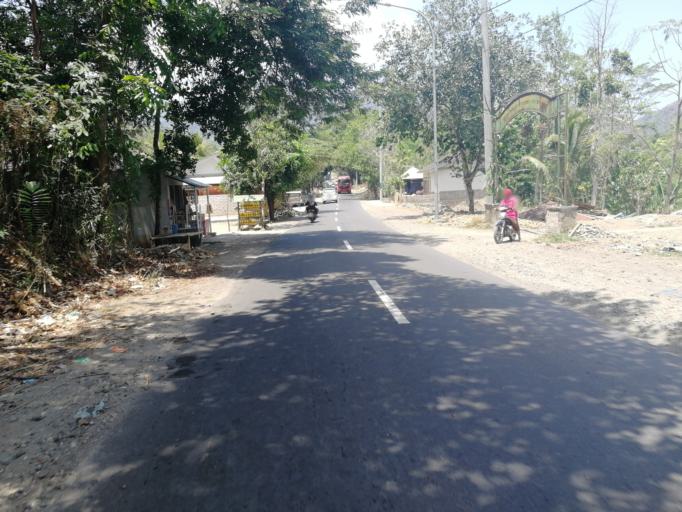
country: ID
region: West Nusa Tenggara
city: Karangsubagan
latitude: -8.4375
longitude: 116.0865
